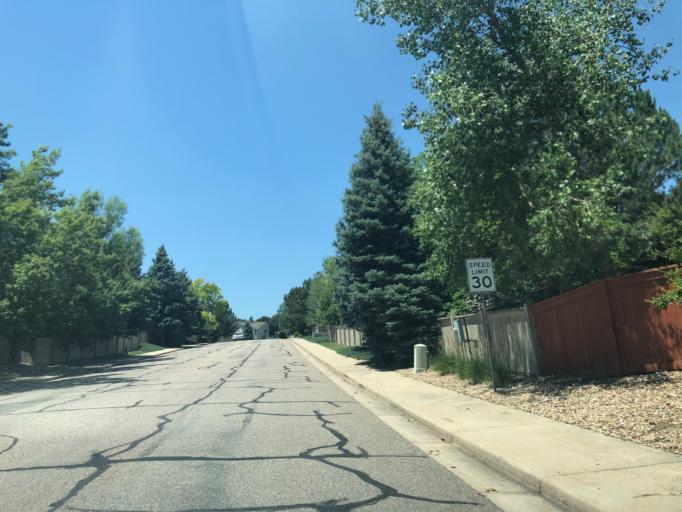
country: US
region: Colorado
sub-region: Arapahoe County
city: Dove Valley
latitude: 39.6217
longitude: -104.7546
